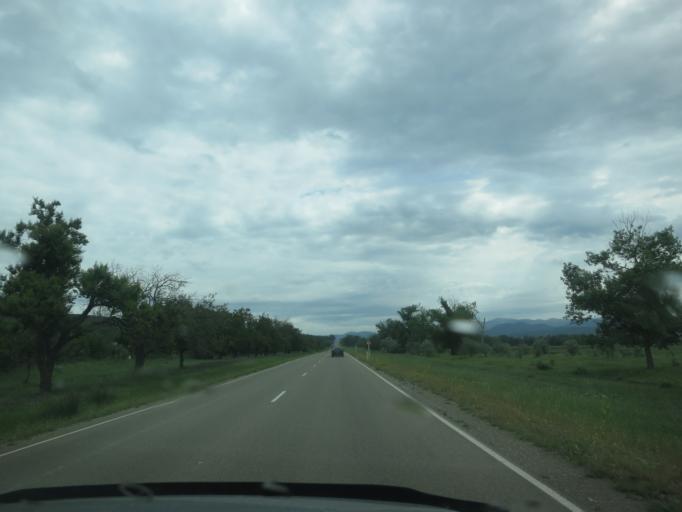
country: GE
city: Didi Lilo
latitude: 41.7415
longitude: 45.1295
